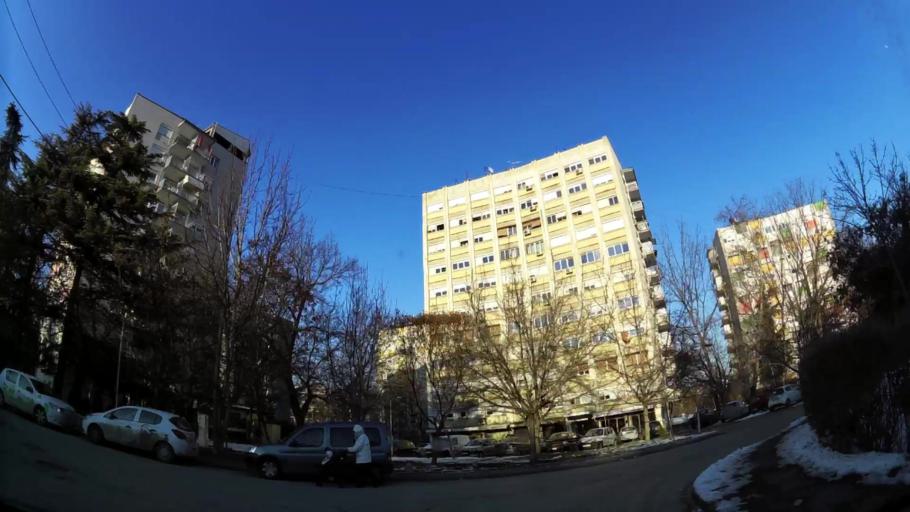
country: MK
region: Karpos
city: Skopje
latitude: 41.9954
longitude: 21.3970
